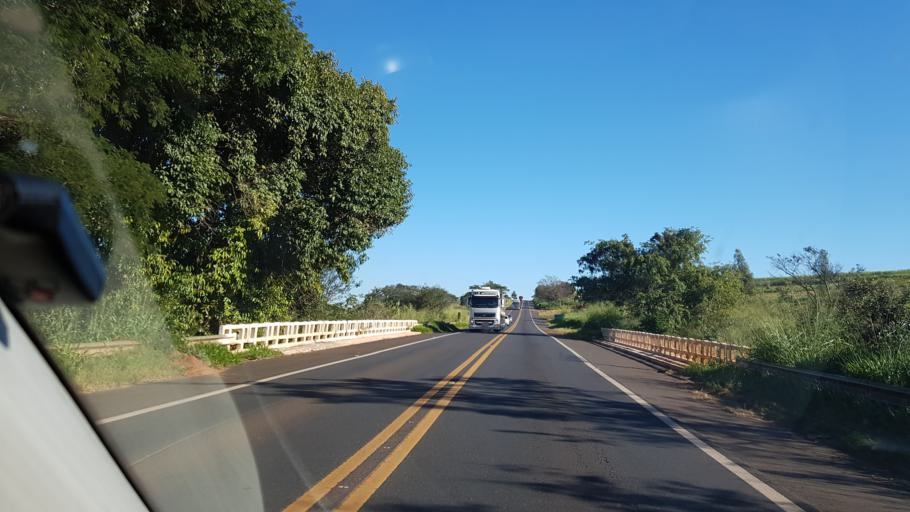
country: BR
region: Sao Paulo
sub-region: Assis
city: Assis
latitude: -22.6106
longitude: -50.4667
